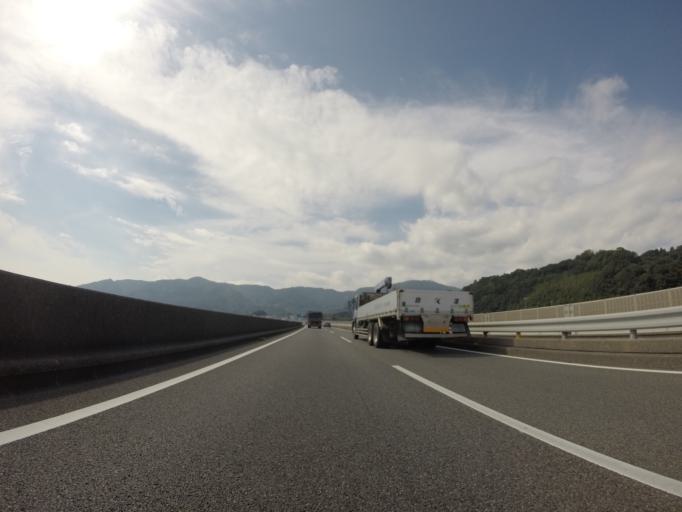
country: JP
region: Shizuoka
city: Fujinomiya
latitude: 35.1124
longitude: 138.5803
